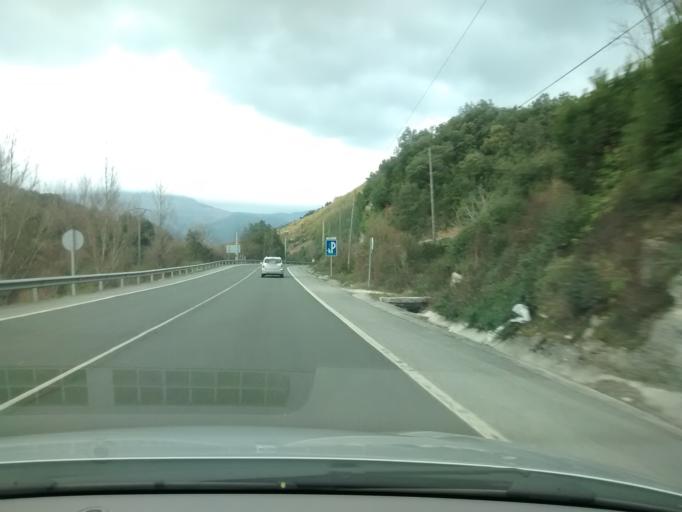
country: ES
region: Castille and Leon
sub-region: Provincia de Burgos
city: Villasana de Mena
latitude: 43.1330
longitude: -3.2626
